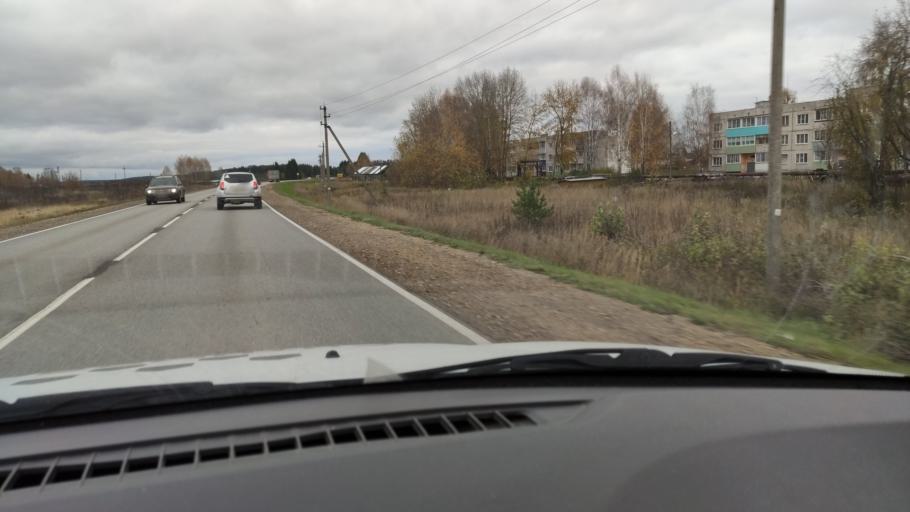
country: RU
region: Kirov
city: Slobodskoy
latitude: 58.7818
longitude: 50.4297
